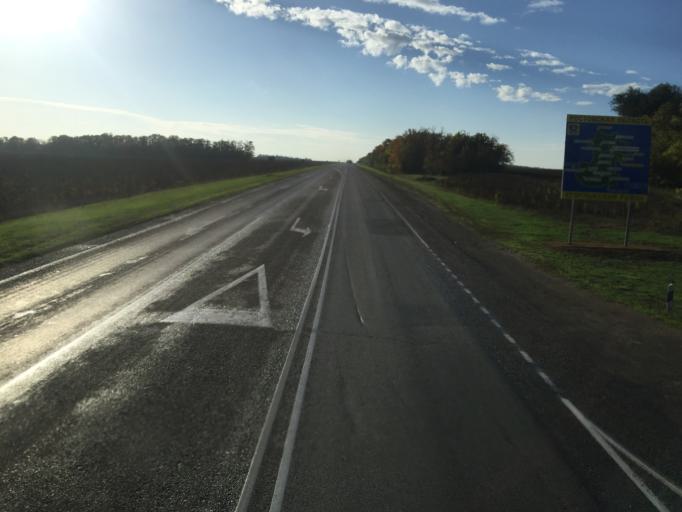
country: RU
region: Rostov
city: Mechetinskaya
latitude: 46.7140
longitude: 40.4933
